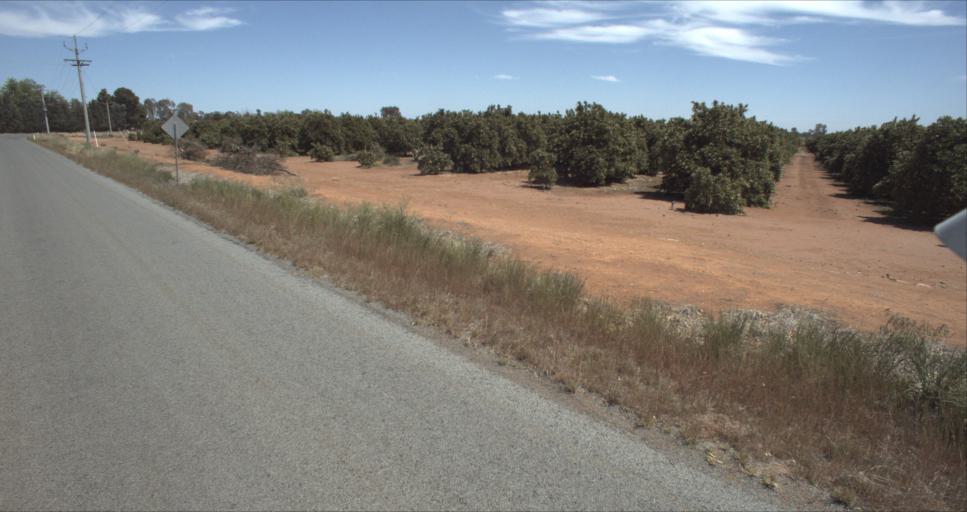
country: AU
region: New South Wales
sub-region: Leeton
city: Leeton
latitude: -34.5658
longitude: 146.4511
